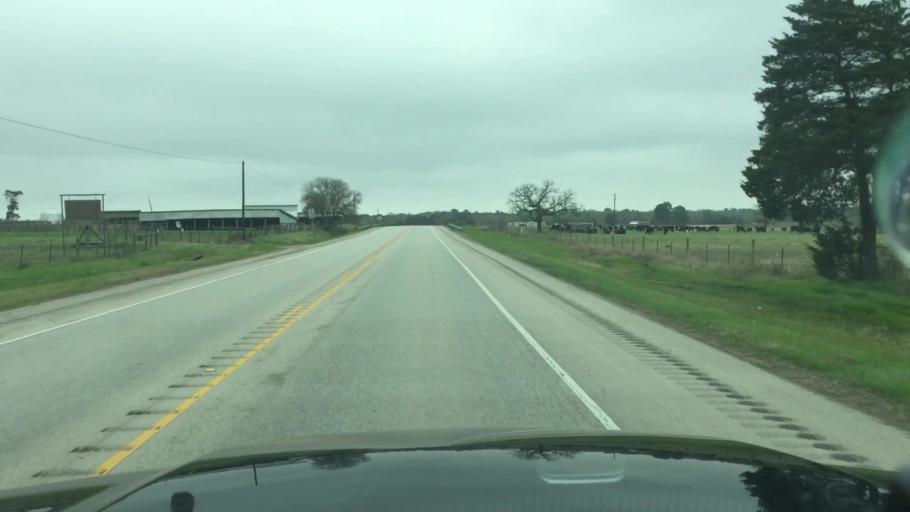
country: US
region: Texas
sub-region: Lee County
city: Giddings
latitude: 30.0597
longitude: -96.9152
